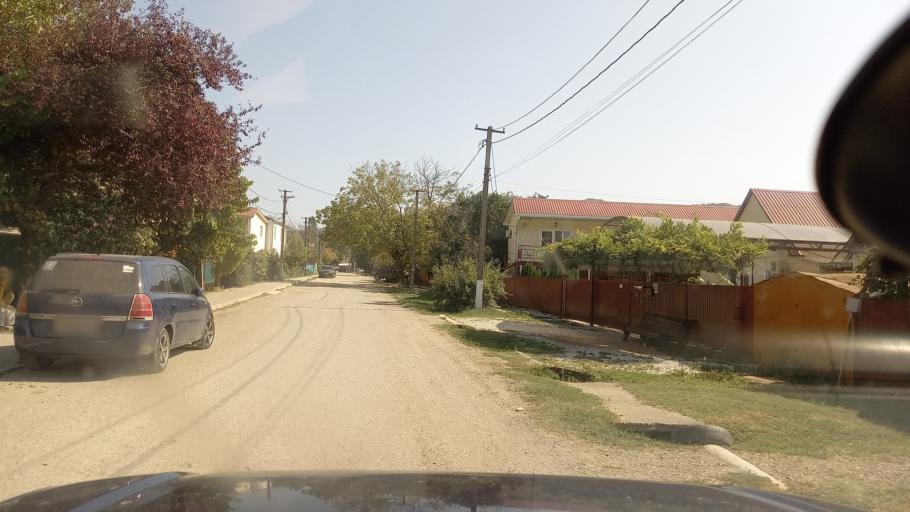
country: RU
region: Krasnodarskiy
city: Arkhipo-Osipovka
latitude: 44.3651
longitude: 38.5258
